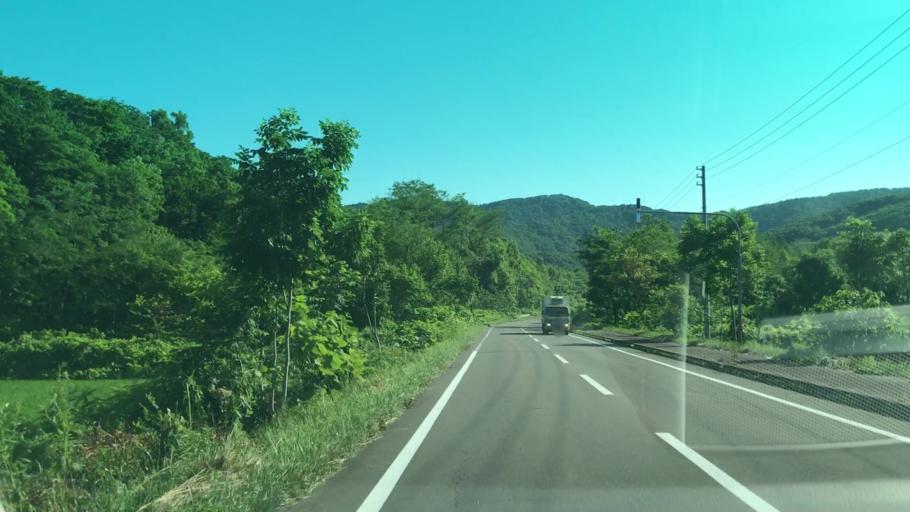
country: JP
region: Hokkaido
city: Yoichi
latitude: 43.0723
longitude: 140.7103
